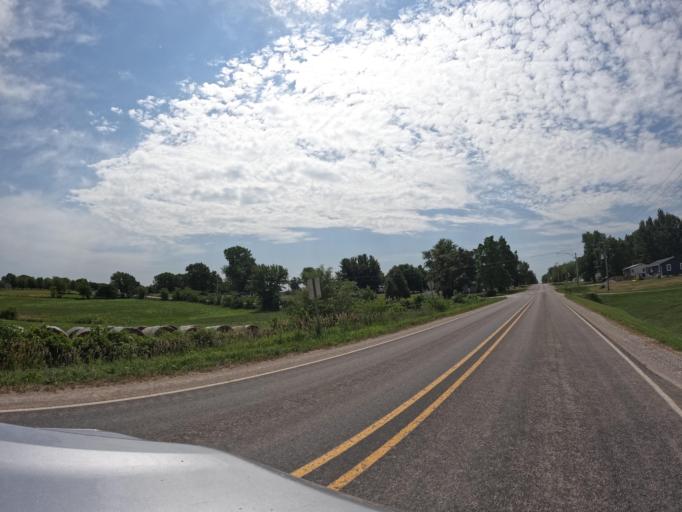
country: US
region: Iowa
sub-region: Appanoose County
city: Centerville
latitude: 40.7872
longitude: -92.9447
